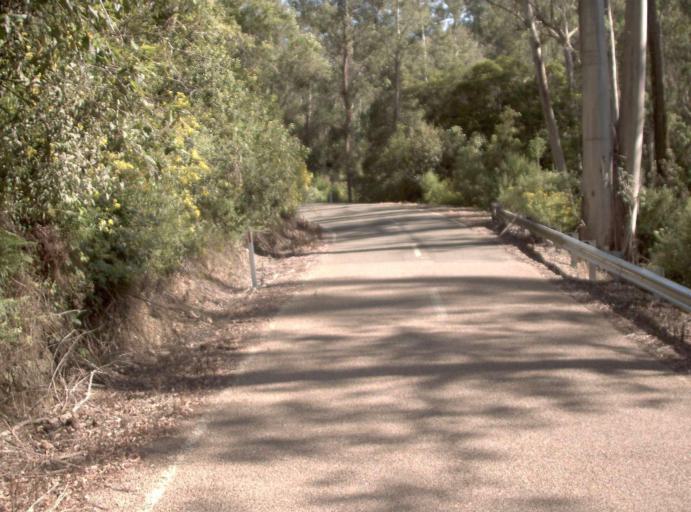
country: AU
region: Victoria
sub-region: East Gippsland
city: Lakes Entrance
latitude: -37.4932
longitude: 148.5555
